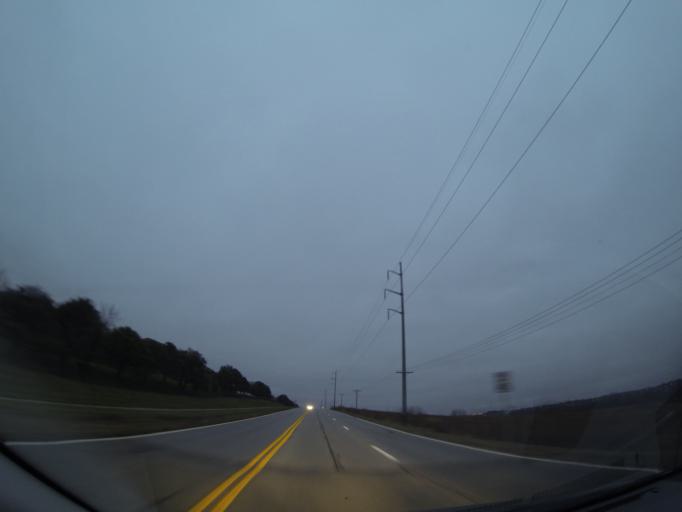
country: US
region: Nebraska
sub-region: Douglas County
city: Elkhorn
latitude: 41.2709
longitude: -96.1772
